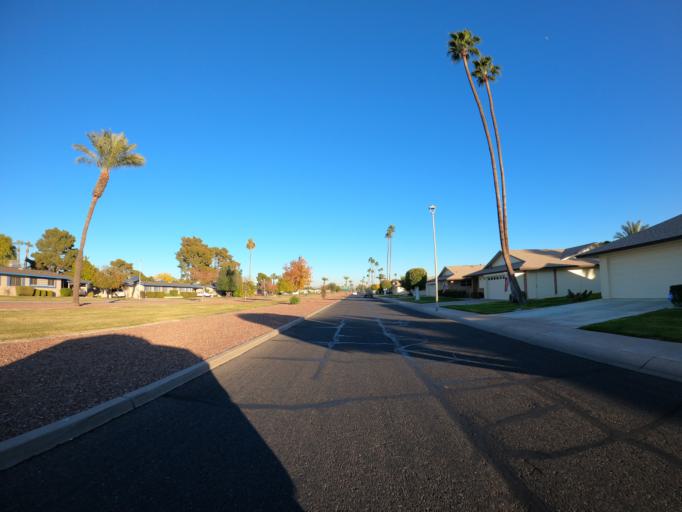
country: US
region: Arizona
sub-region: Maricopa County
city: Youngtown
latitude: 33.5799
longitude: -112.2973
